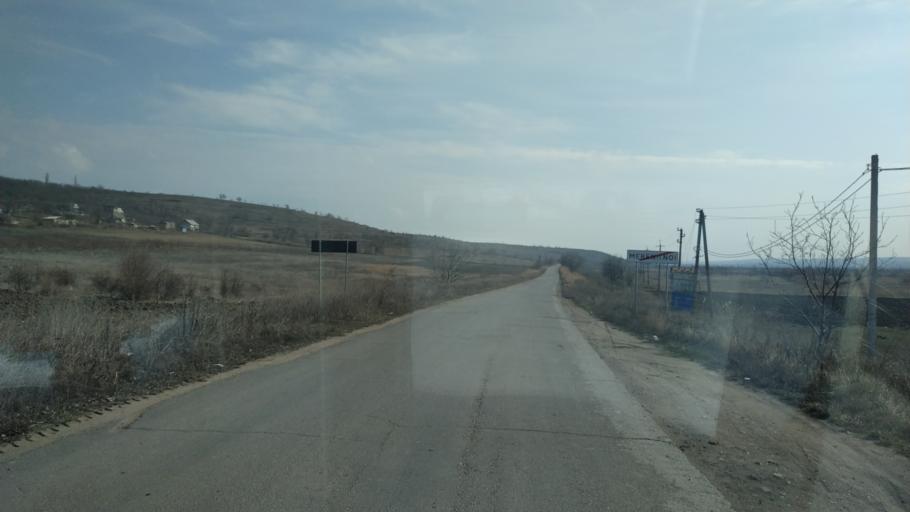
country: MD
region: Chisinau
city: Singera
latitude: 46.9258
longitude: 29.0770
